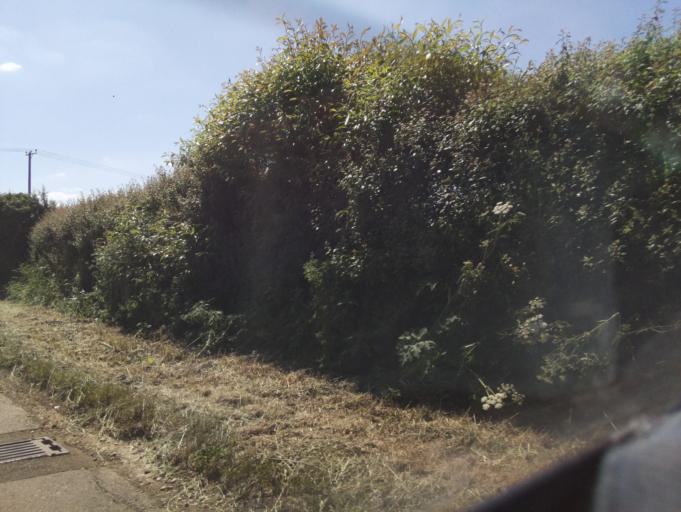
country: GB
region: England
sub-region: Wiltshire
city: Lyneham
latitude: 51.4790
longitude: -1.9499
